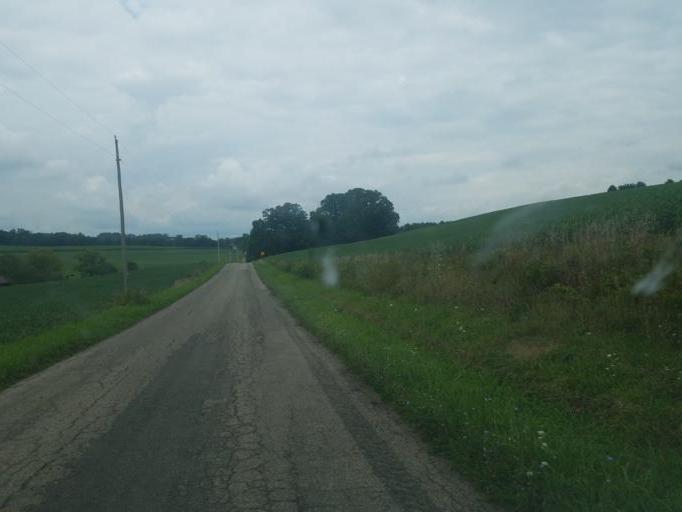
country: US
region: Ohio
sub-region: Knox County
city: Danville
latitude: 40.4990
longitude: -82.3061
